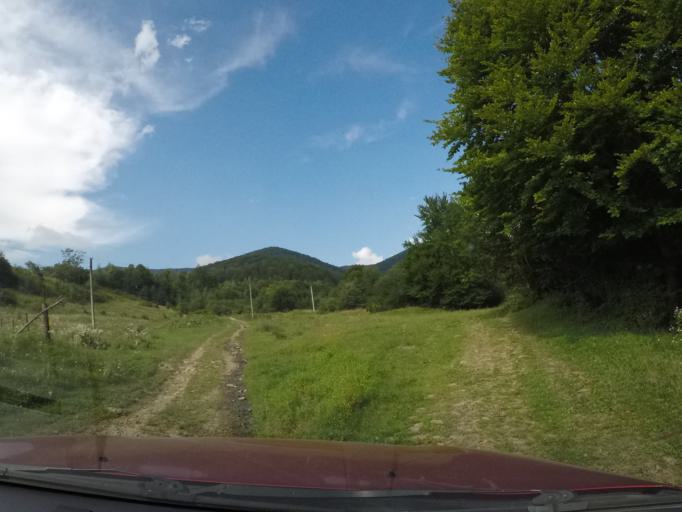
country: PL
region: Subcarpathian Voivodeship
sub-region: Powiat bieszczadzki
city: Lutowiska
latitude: 49.0301
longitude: 22.6482
